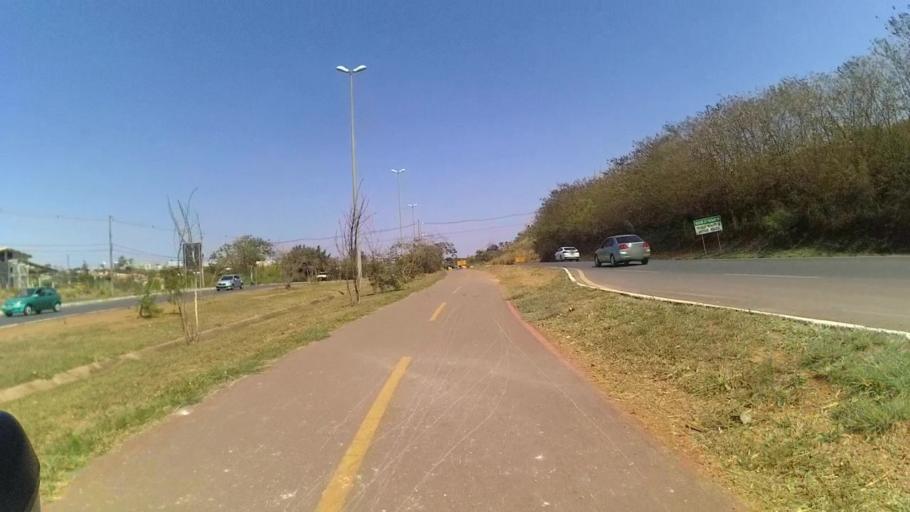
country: BR
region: Federal District
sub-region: Brasilia
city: Brasilia
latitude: -15.7169
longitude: -47.8664
